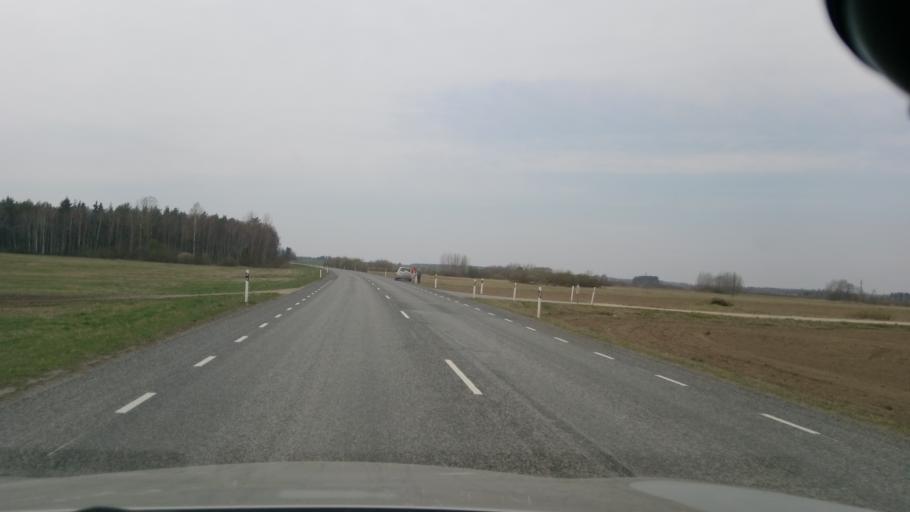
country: EE
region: Jaervamaa
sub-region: Tueri vald
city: Sarevere
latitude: 58.7747
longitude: 25.5119
